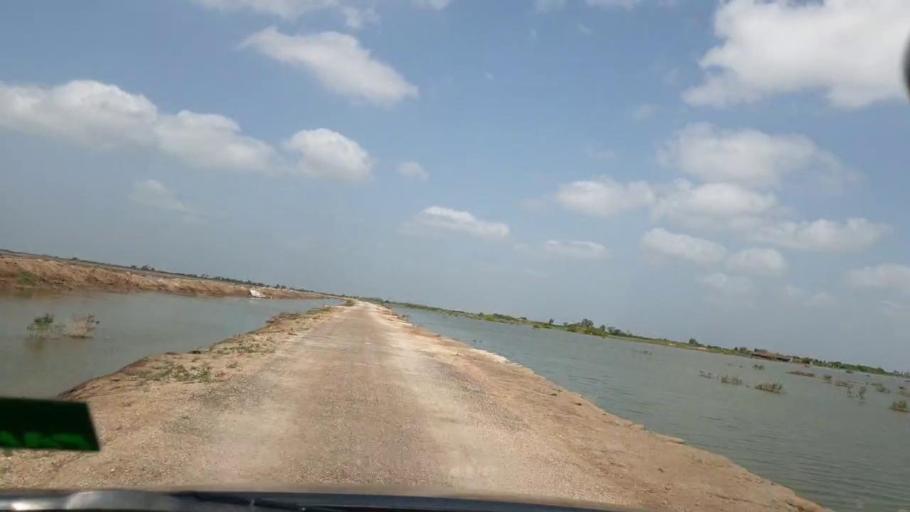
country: PK
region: Sindh
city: Kadhan
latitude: 24.5901
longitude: 69.1363
